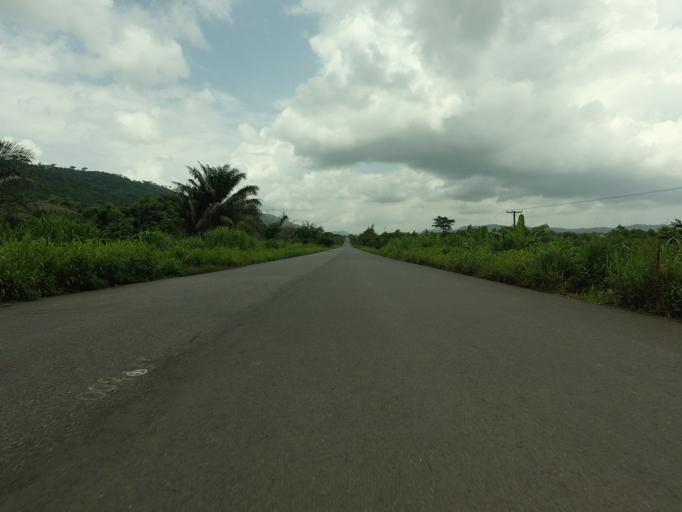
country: GH
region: Volta
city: Ho
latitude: 6.6161
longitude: 0.3039
